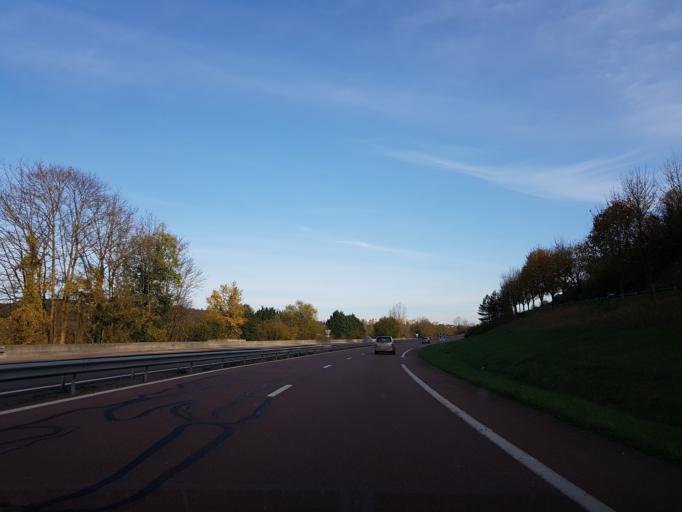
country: FR
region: Bourgogne
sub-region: Departement de la Cote-d'Or
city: Plombieres-les-Dijon
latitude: 47.3378
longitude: 4.9611
